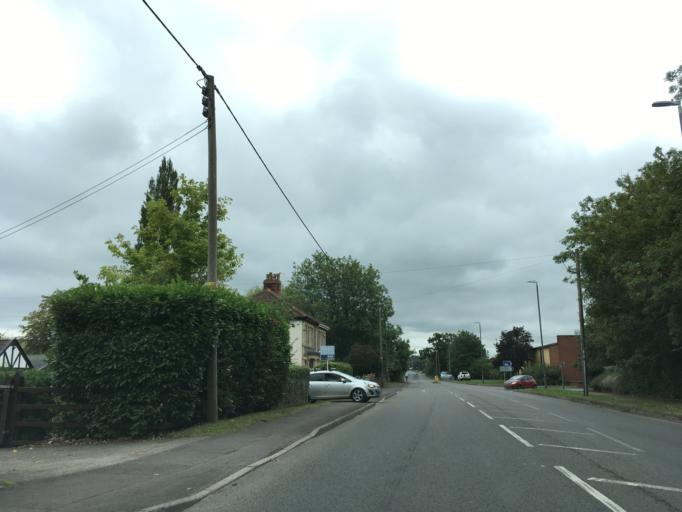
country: GB
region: England
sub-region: South Gloucestershire
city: Bitton
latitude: 51.4507
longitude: -2.4633
